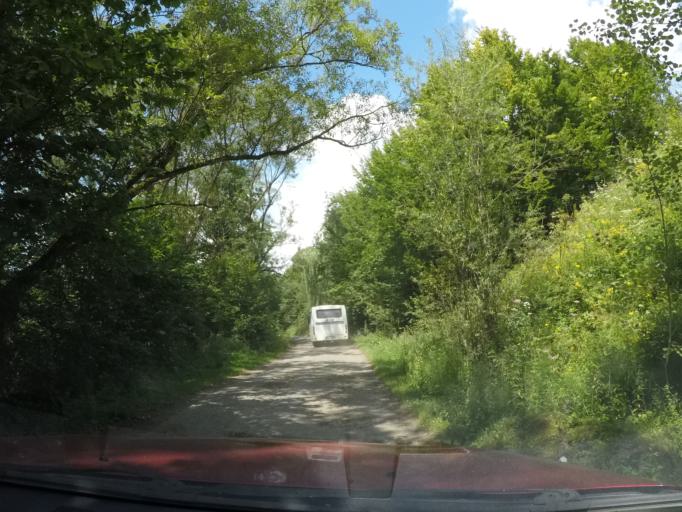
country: UA
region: Zakarpattia
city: Velykyi Bereznyi
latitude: 49.0270
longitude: 22.6008
